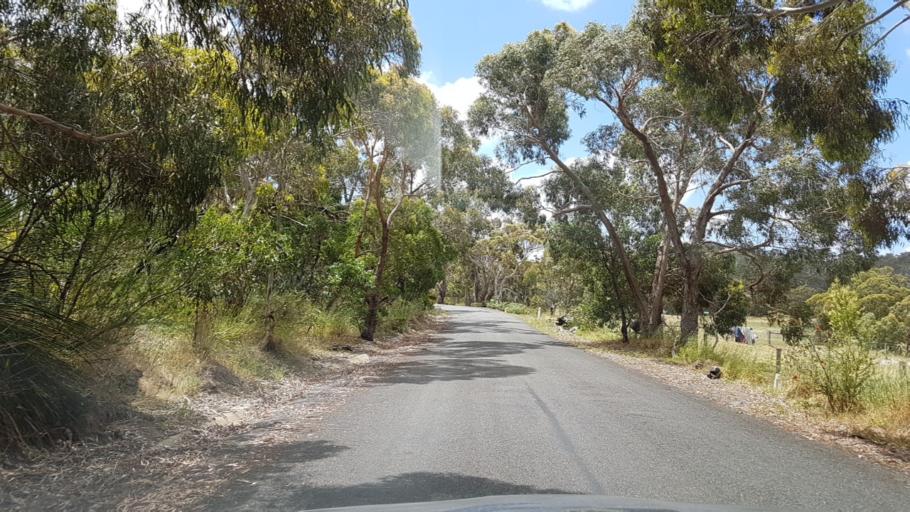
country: AU
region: South Australia
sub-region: Victor Harbor
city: Victor Harbor
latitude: -35.4576
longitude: 138.5921
